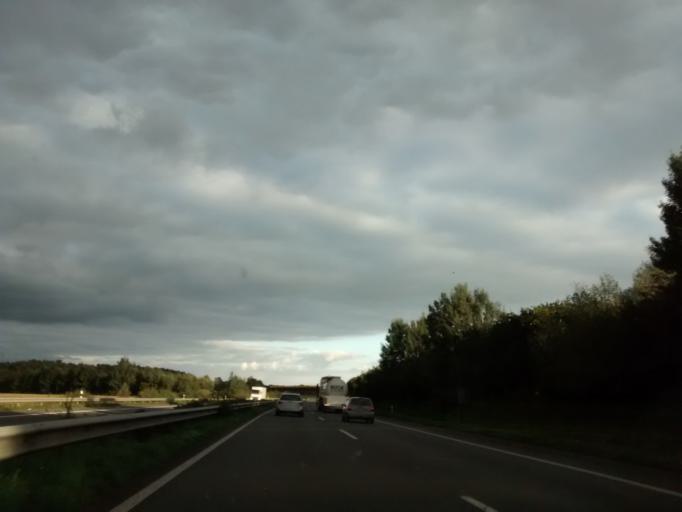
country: DE
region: Lower Saxony
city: Salzbergen
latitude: 52.3425
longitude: 7.3962
